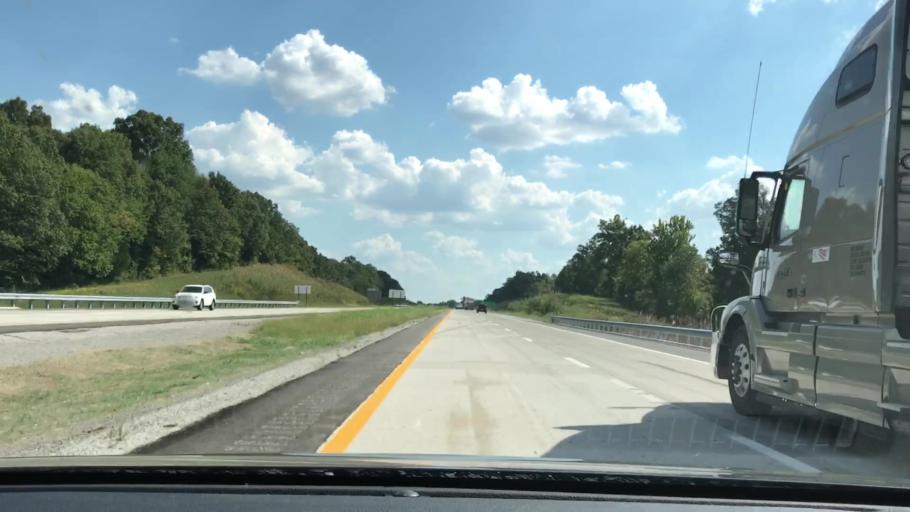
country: US
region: Kentucky
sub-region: Ohio County
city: Oak Grove
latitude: 37.3772
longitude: -86.8049
